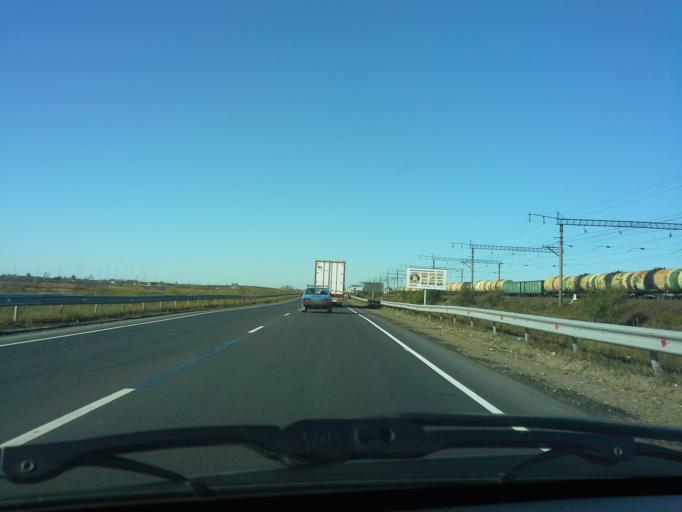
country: RU
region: Jewish Autonomous Oblast
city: Priamurskiy
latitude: 48.5266
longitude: 134.9405
